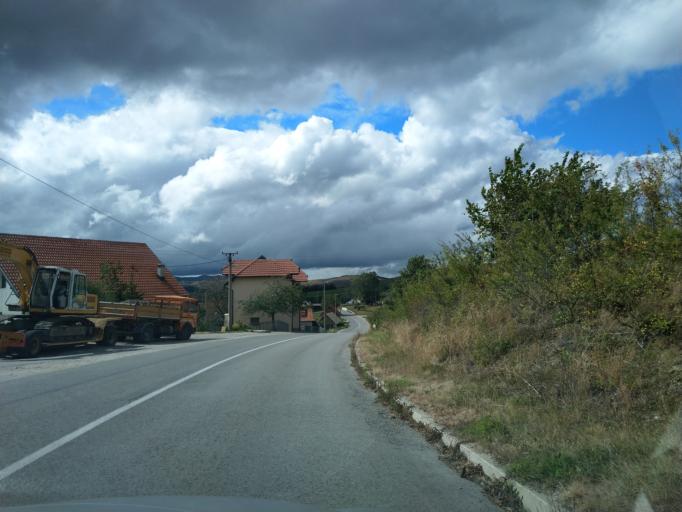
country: RS
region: Central Serbia
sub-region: Zlatiborski Okrug
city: Cajetina
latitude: 43.7147
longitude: 19.7720
